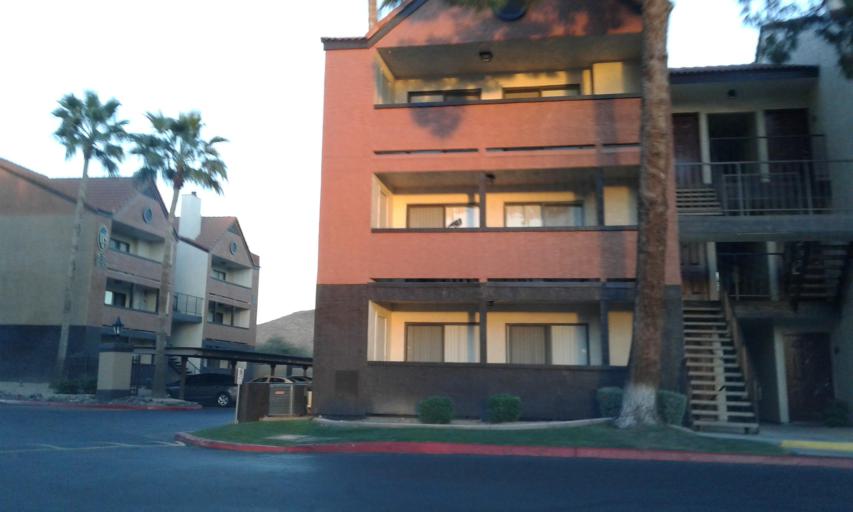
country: US
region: Arizona
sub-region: Maricopa County
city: Glendale
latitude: 33.5959
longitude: -112.1142
